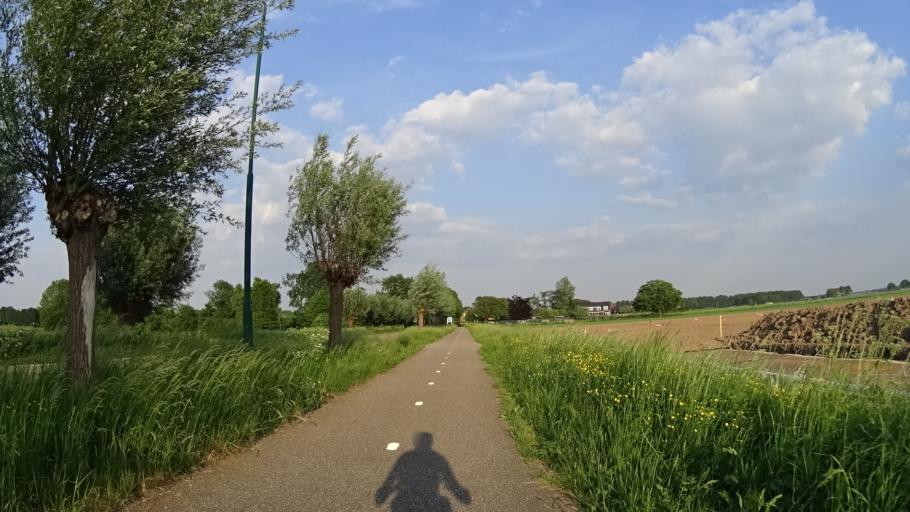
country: NL
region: North Brabant
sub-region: Gemeente Heusden
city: Heusden
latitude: 51.7264
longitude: 5.1480
